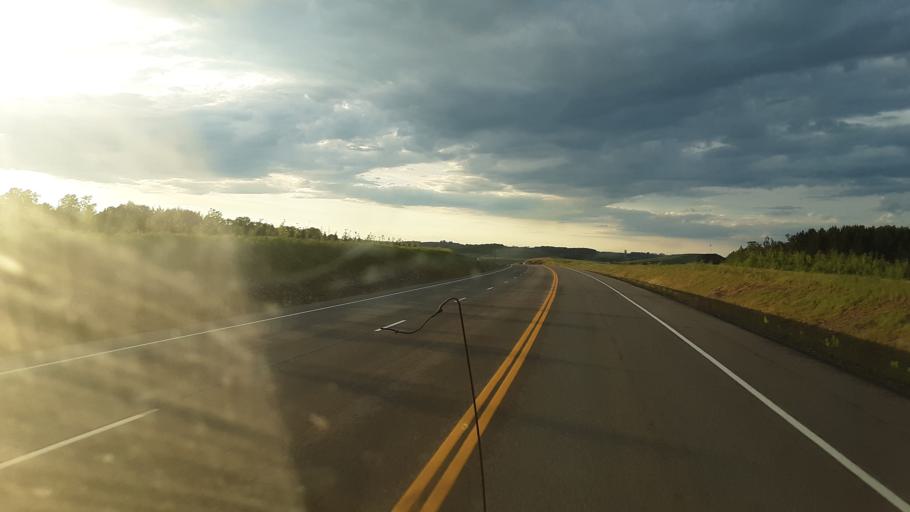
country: US
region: Maine
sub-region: Aroostook County
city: Presque Isle
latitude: 46.6832
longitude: -67.9750
